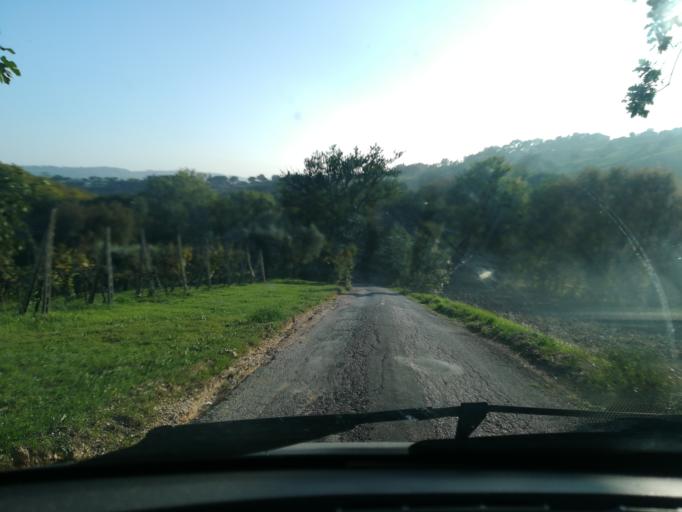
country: IT
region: The Marches
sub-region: Provincia di Macerata
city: Macerata
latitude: 43.2843
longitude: 13.4557
